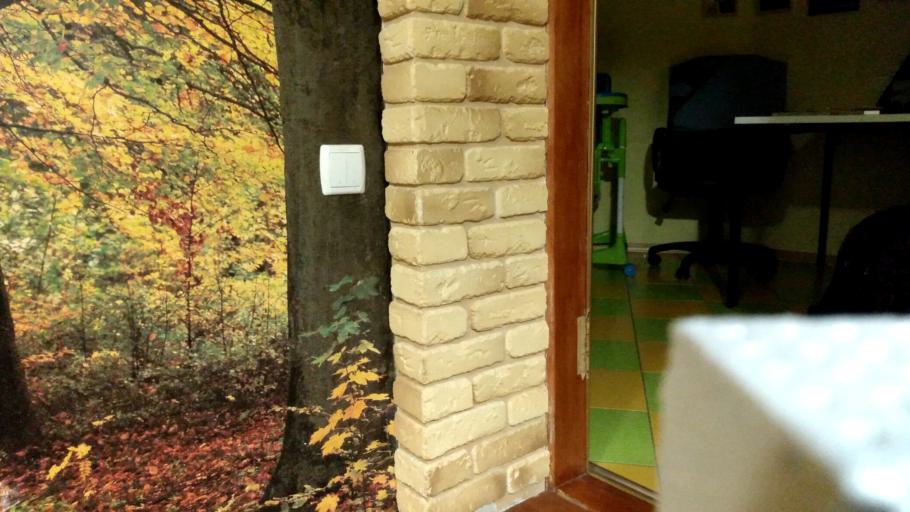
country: RU
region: Arkhangelskaya
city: Kargopol'
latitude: 61.5212
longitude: 37.7725
